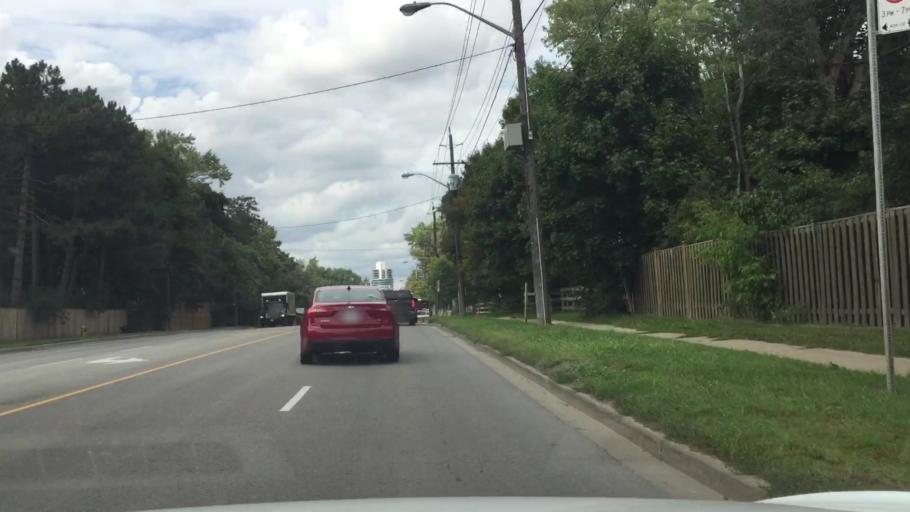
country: CA
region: Ontario
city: Willowdale
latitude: 43.7571
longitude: -79.3859
